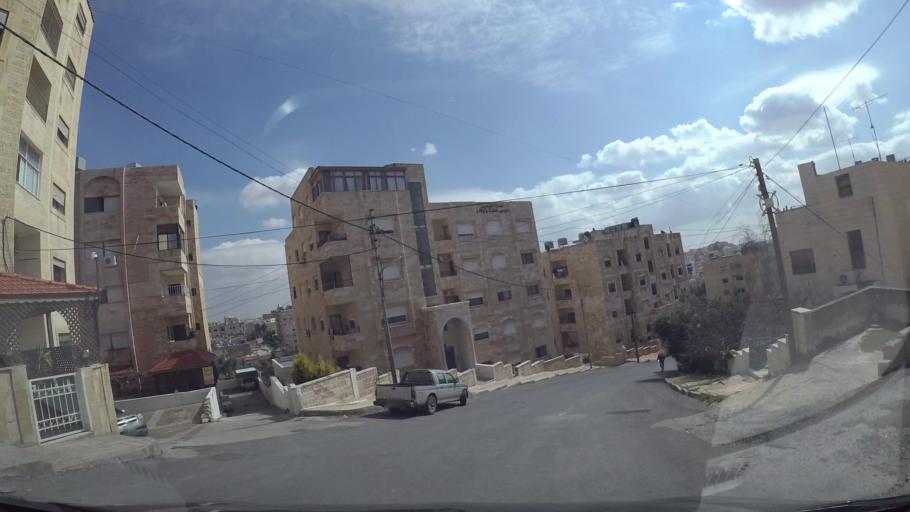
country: JO
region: Amman
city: Al Jubayhah
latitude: 31.9928
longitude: 35.9064
